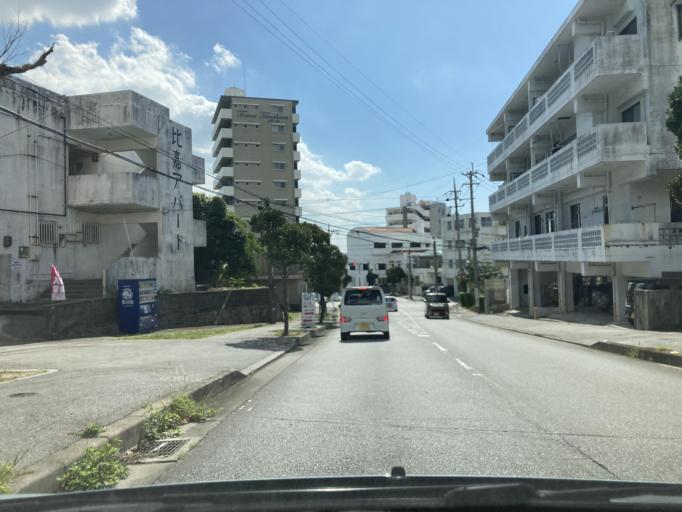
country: JP
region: Okinawa
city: Ginowan
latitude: 26.2448
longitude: 127.7557
